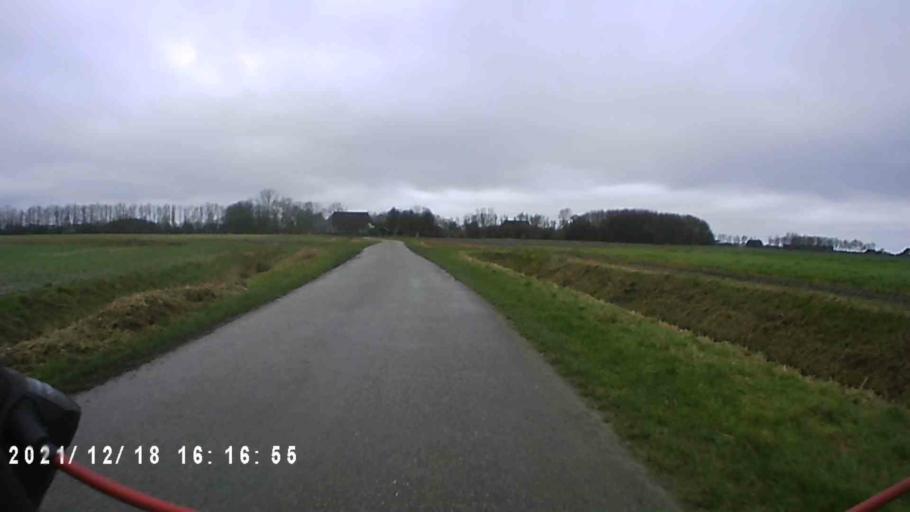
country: NL
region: Friesland
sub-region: Gemeente Dongeradeel
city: Anjum
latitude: 53.3737
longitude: 6.0595
